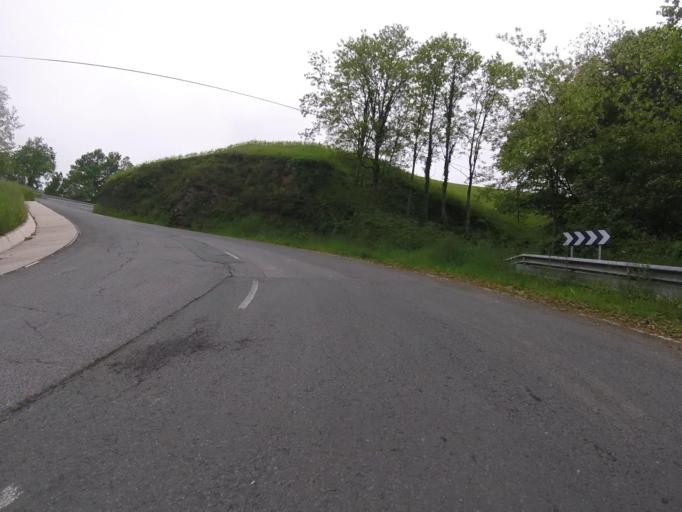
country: ES
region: Navarre
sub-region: Provincia de Navarra
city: Zugarramurdi
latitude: 43.2664
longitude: -1.4975
